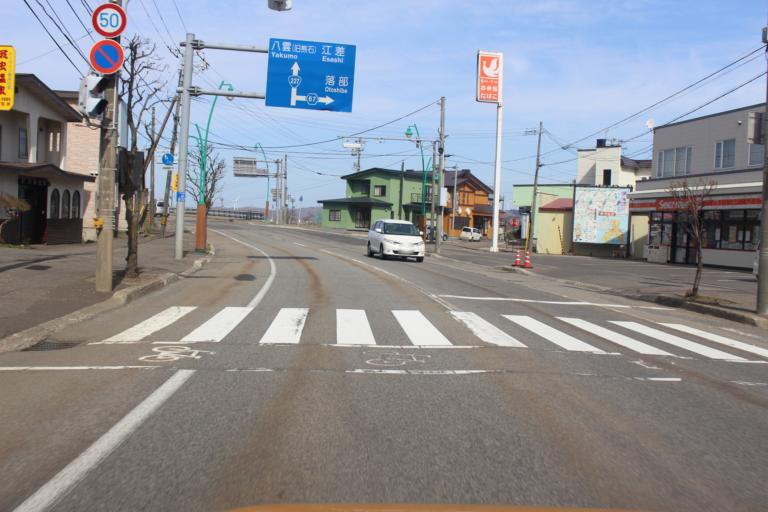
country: JP
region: Hokkaido
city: Kamiiso
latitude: 41.9168
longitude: 140.2237
